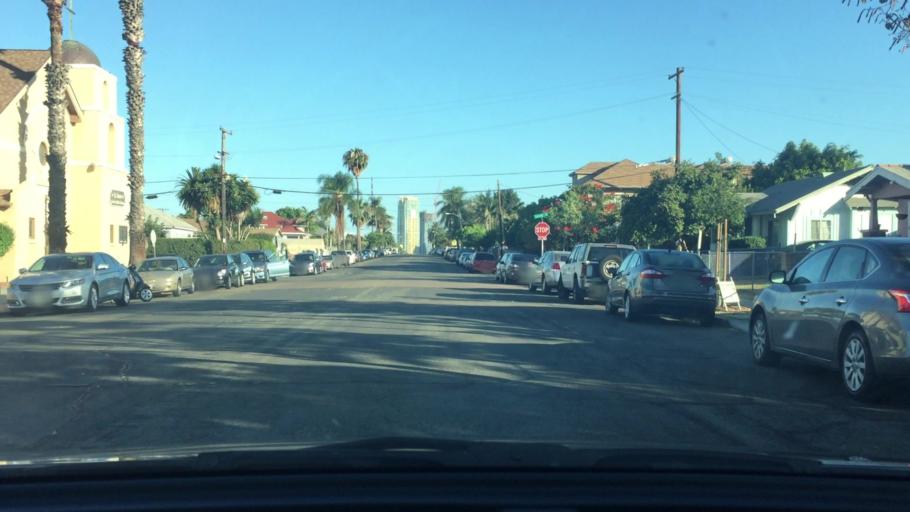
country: US
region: California
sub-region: San Diego County
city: San Diego
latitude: 32.6990
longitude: -117.1348
